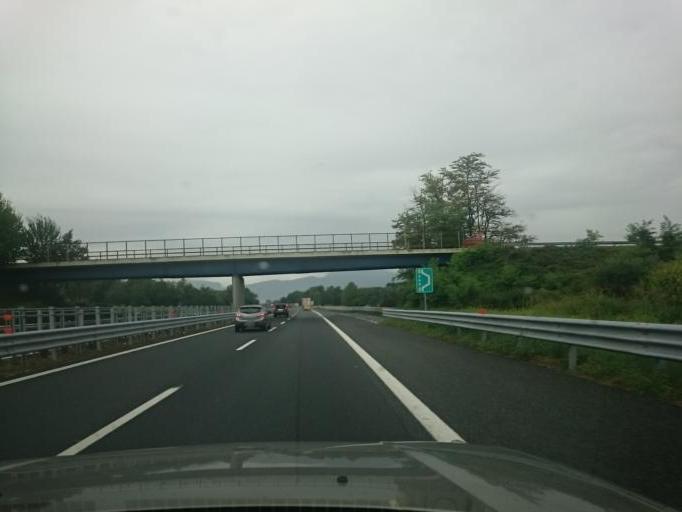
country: IT
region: Friuli Venezia Giulia
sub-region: Provincia di Udine
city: Collofedo di Monte Albano
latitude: 46.1783
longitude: 13.1371
